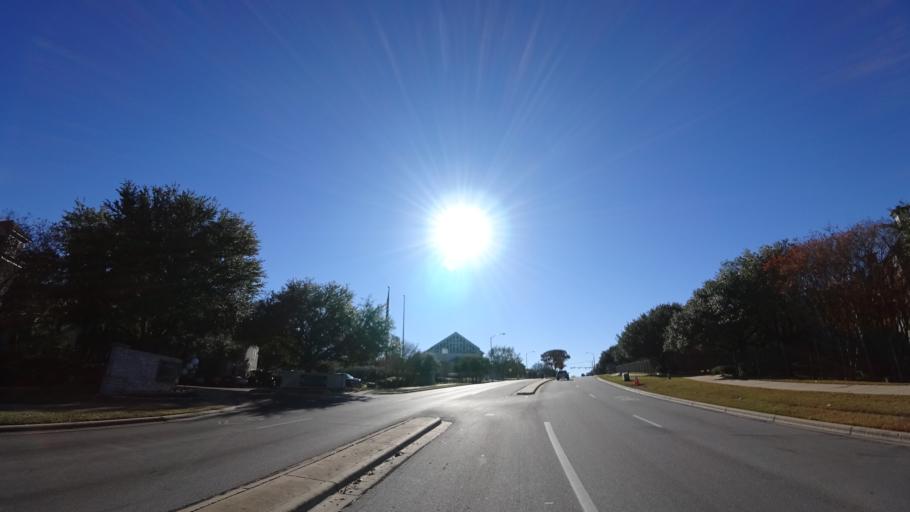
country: US
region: Texas
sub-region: Travis County
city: Wells Branch
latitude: 30.4042
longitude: -97.6986
